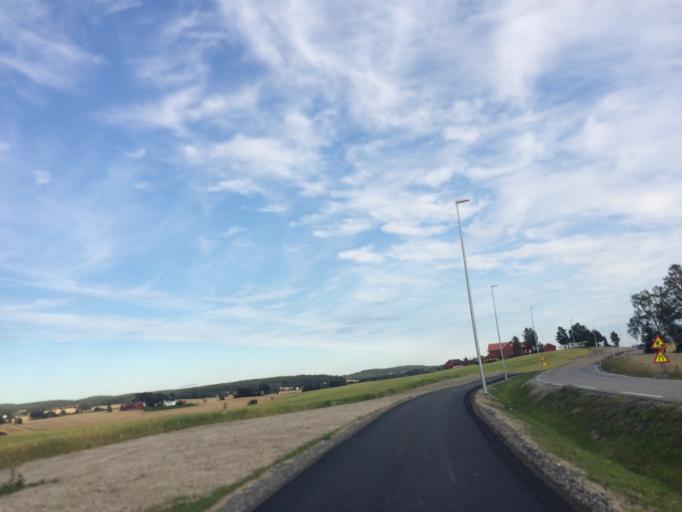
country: NO
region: Akershus
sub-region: Ski
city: Ski
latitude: 59.6958
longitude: 10.8577
